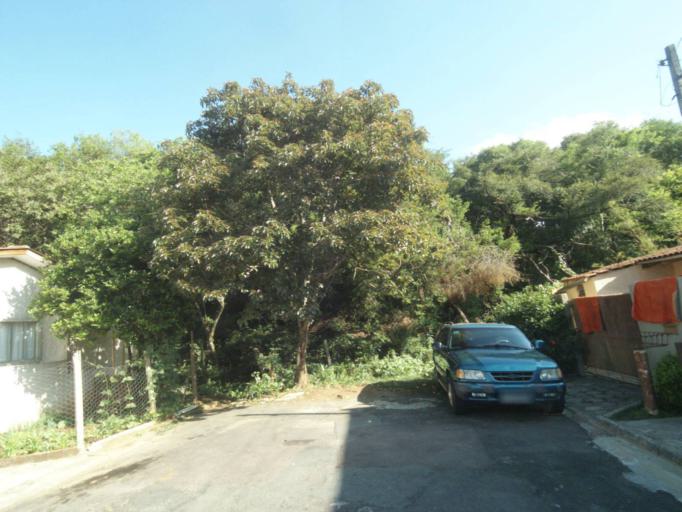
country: BR
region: Parana
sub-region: Curitiba
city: Curitiba
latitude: -25.3954
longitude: -49.3028
